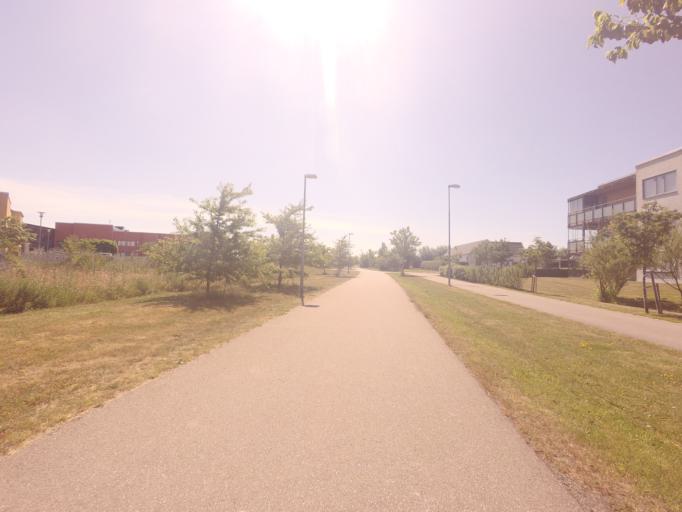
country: SE
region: Skane
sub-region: Vellinge Kommun
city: Hollviken
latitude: 55.4264
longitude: 12.9746
